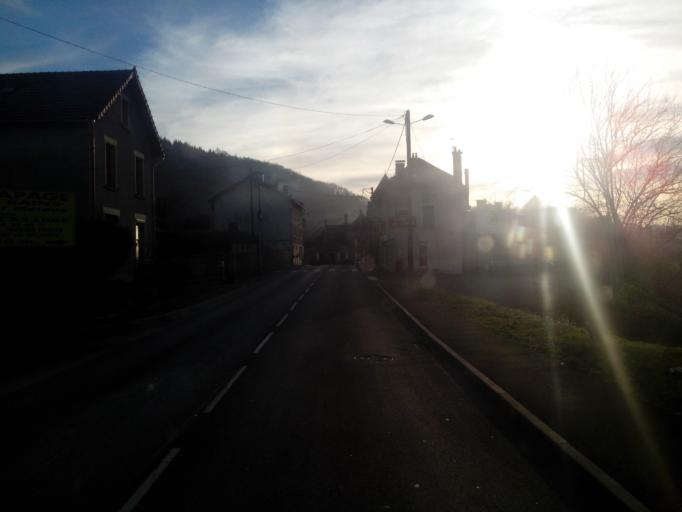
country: FR
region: Limousin
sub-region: Departement de la Correze
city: Bort-les-Orgues
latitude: 45.3829
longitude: 2.4874
